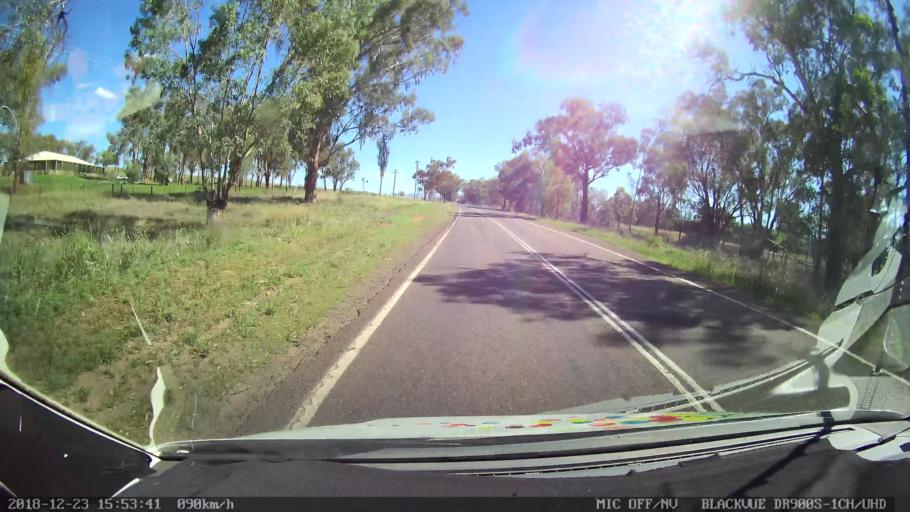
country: AU
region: New South Wales
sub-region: Tamworth Municipality
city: Phillip
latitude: -31.1364
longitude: 150.8796
